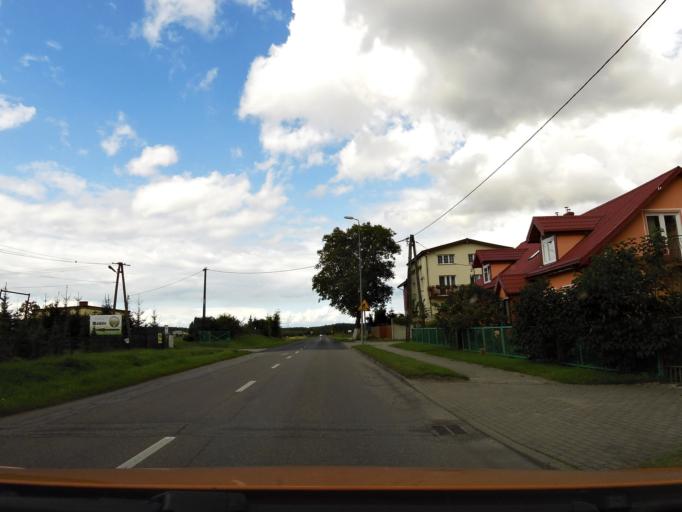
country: PL
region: West Pomeranian Voivodeship
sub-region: Powiat kolobrzeski
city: Kolobrzeg
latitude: 54.0928
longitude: 15.5754
